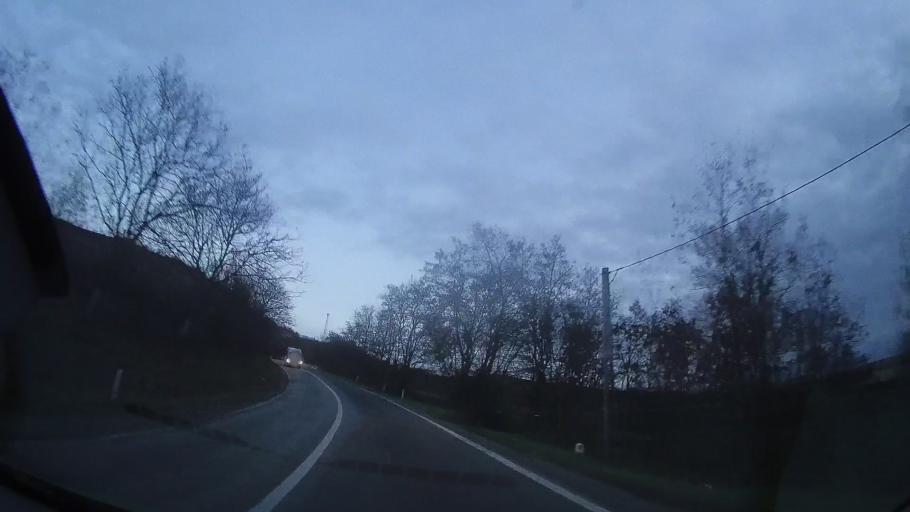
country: RO
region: Cluj
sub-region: Comuna Mociu
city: Mociu
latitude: 46.8034
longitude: 23.9923
